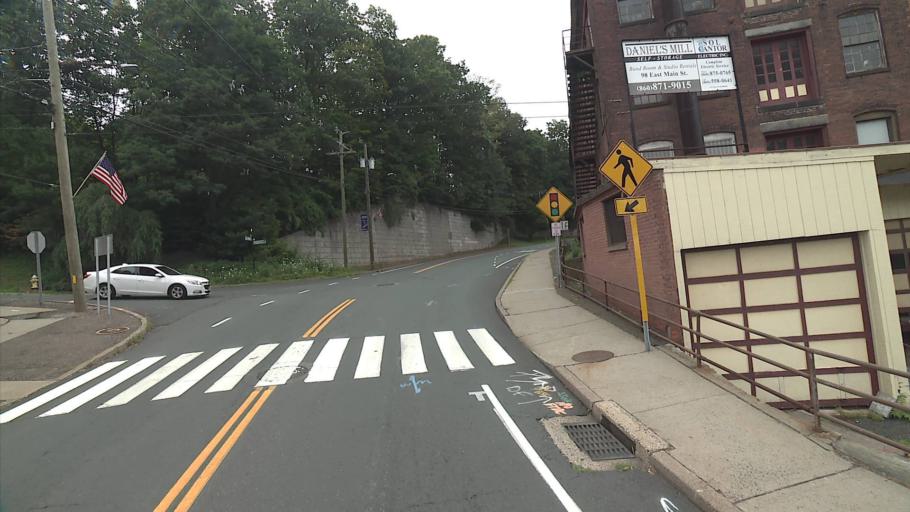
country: US
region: Connecticut
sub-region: Tolland County
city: Rockville
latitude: 41.8681
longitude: -72.4437
